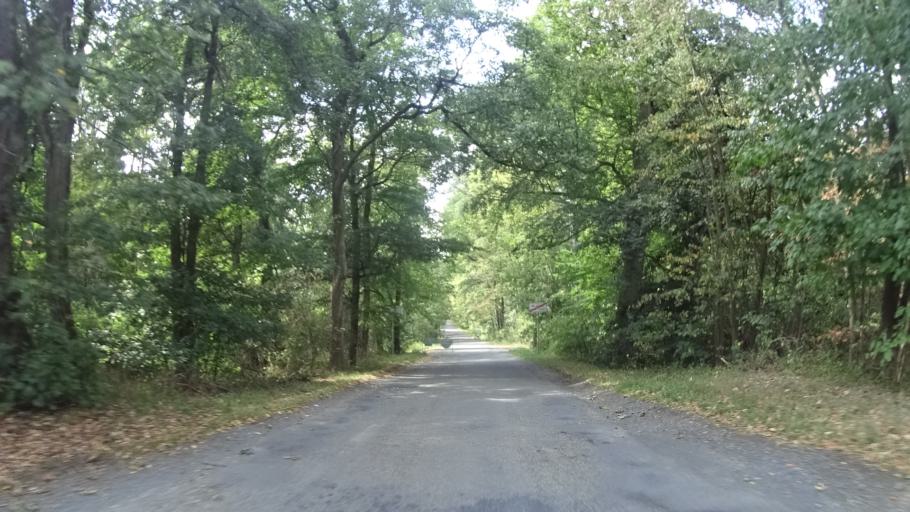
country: CZ
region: Olomoucky
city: Cervenka
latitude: 49.7227
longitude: 17.0266
